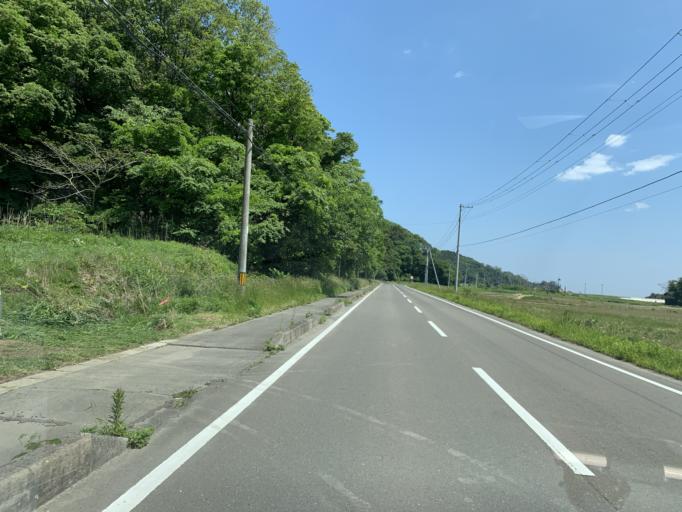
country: JP
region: Miyagi
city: Matsushima
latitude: 38.3318
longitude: 141.1593
